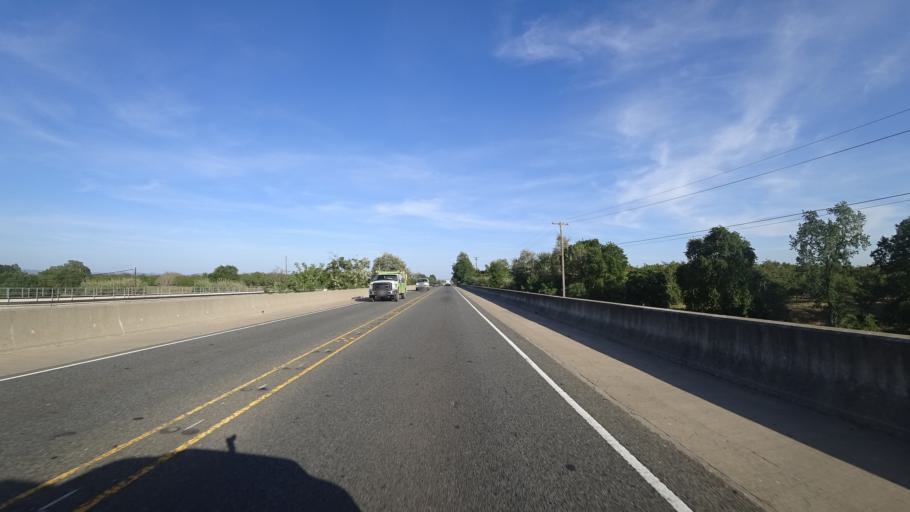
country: US
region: California
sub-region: Yuba County
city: Wheatland
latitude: 38.9999
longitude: -121.4066
